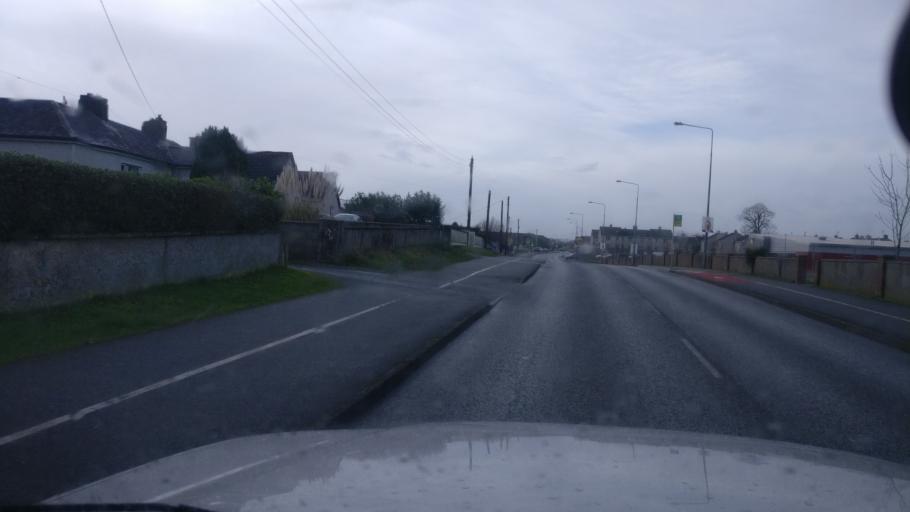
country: IE
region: Leinster
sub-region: Kilkenny
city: Kilkenny
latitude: 52.6635
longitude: -7.2312
